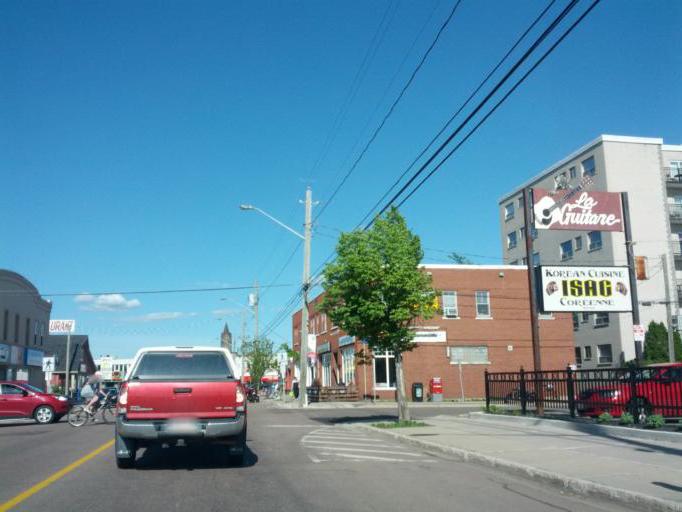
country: CA
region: New Brunswick
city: Moncton
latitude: 46.0897
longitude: -64.7898
